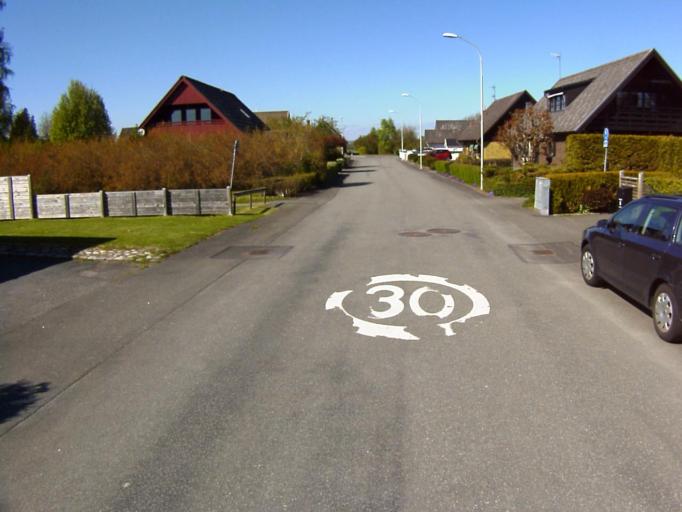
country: SE
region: Skane
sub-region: Kristianstads Kommun
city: Kristianstad
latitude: 56.0333
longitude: 14.2006
